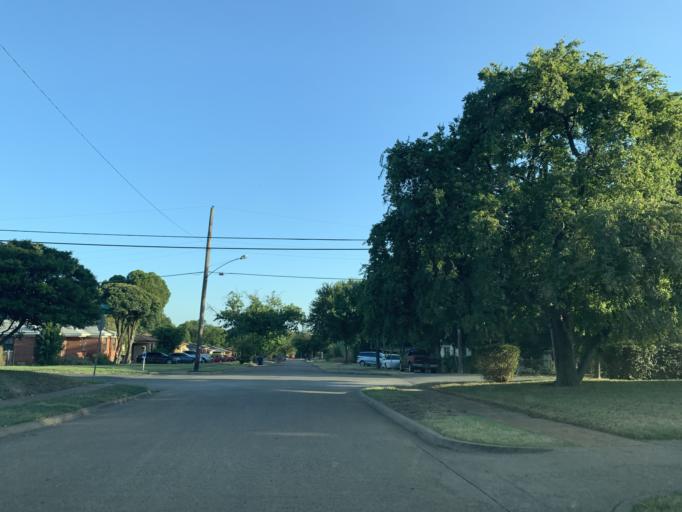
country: US
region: Texas
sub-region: Dallas County
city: Dallas
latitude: 32.6989
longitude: -96.8096
